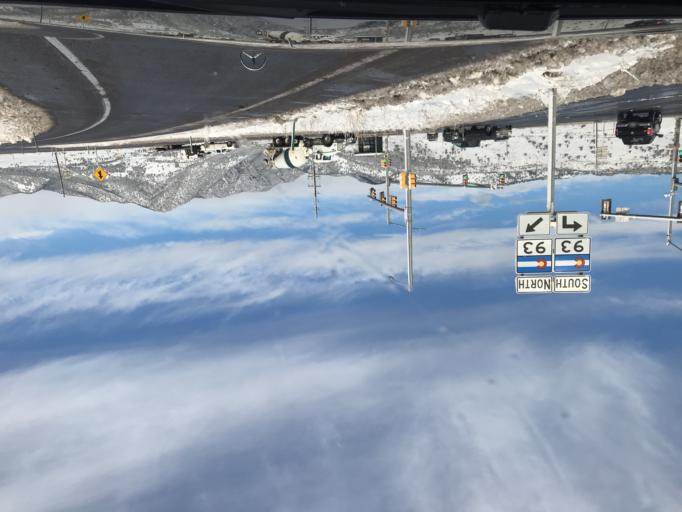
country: US
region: Colorado
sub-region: Jefferson County
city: Golden
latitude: 39.8659
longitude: -105.2393
